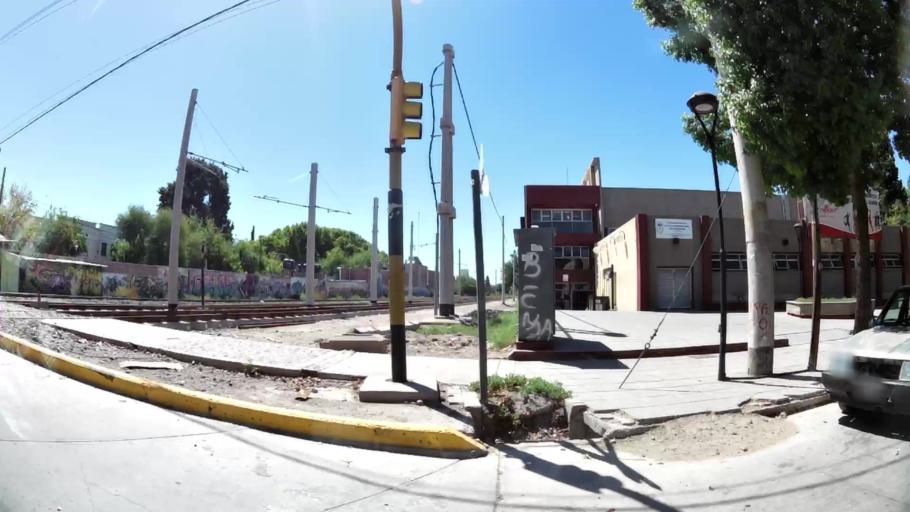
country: AR
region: Mendoza
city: Las Heras
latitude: -32.8517
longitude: -68.8398
